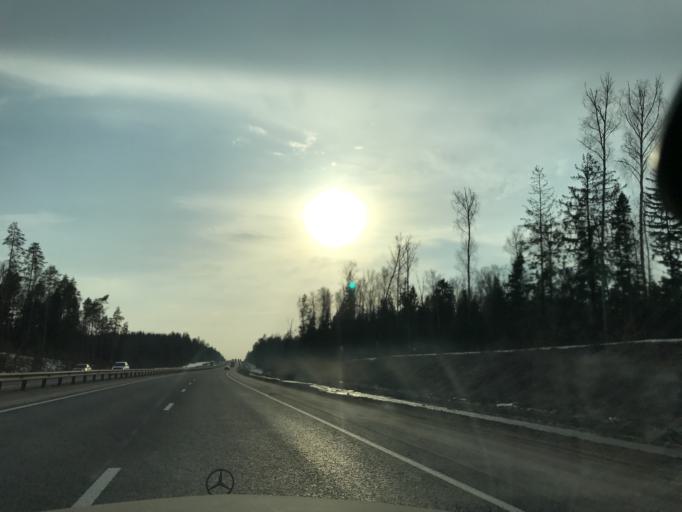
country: RU
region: Vladimir
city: Sudogda
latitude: 56.1469
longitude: 40.9115
